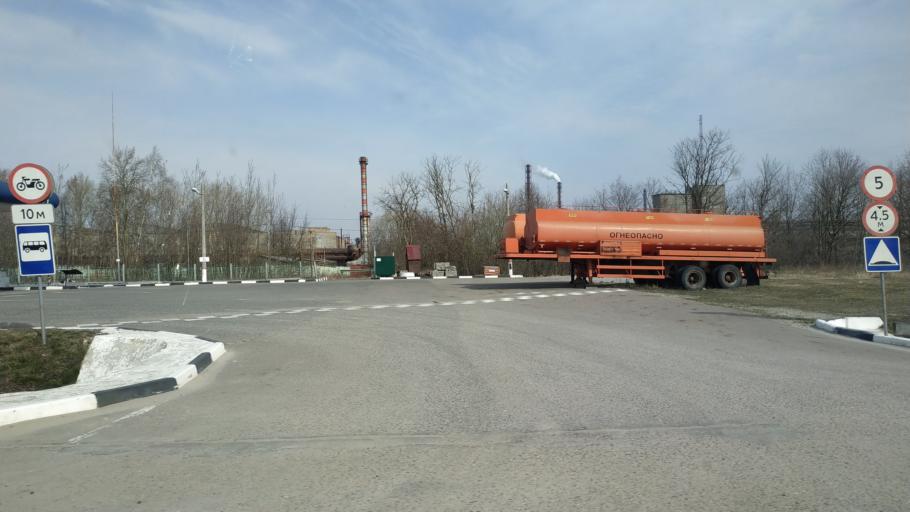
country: RU
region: Moskovskaya
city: Voskresensk
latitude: 55.2887
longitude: 38.6801
